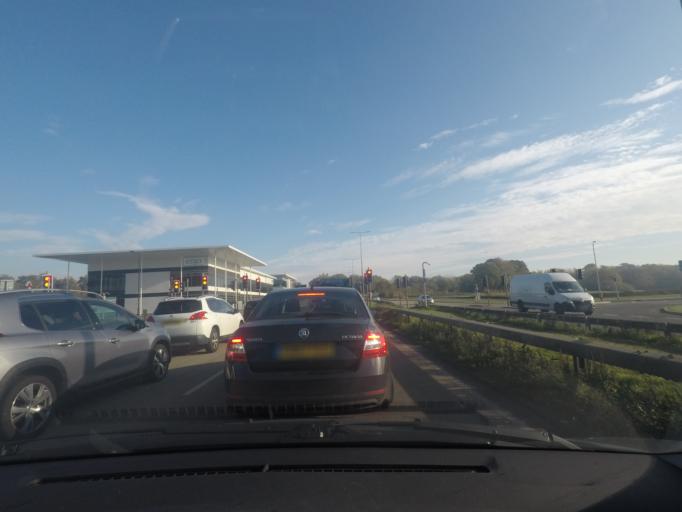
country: GB
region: England
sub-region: East Riding of Yorkshire
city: Hessle
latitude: 53.7235
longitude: -0.4607
